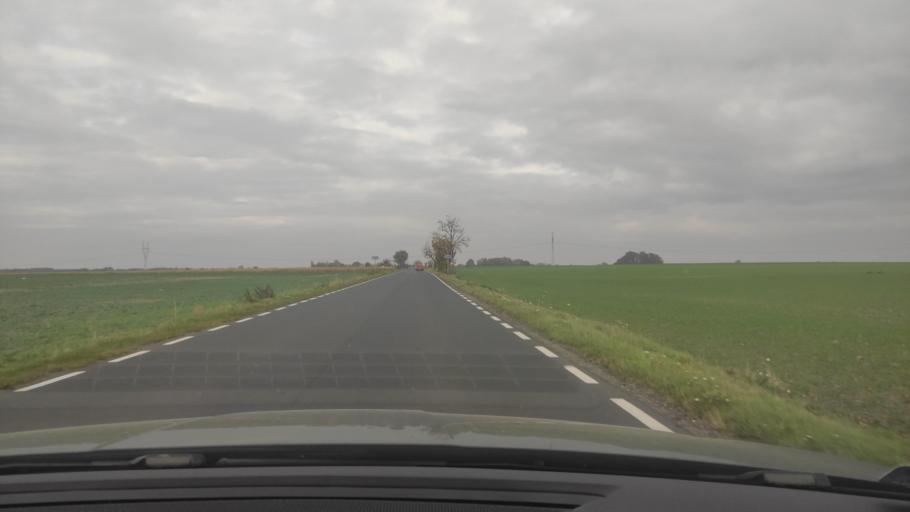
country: PL
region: Greater Poland Voivodeship
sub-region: Powiat poznanski
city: Kostrzyn
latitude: 52.4326
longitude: 17.1609
